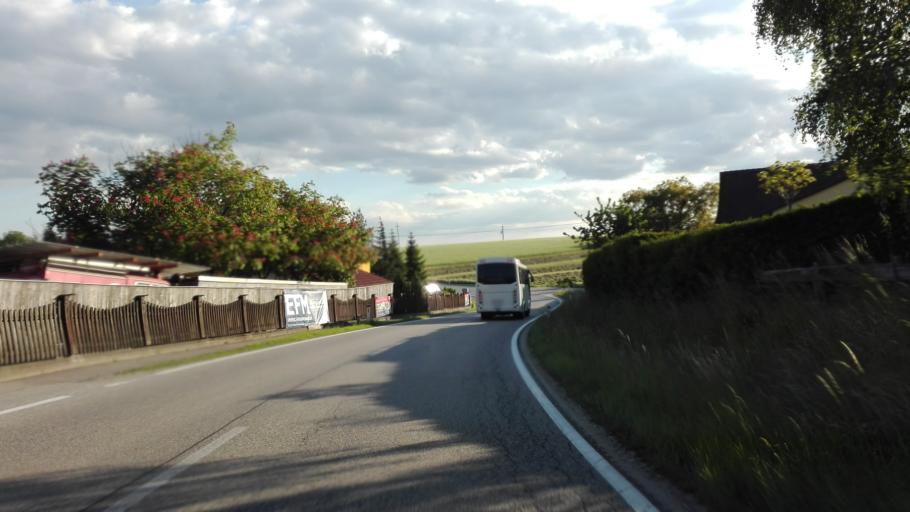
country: AT
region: Upper Austria
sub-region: Politischer Bezirk Urfahr-Umgebung
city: Engerwitzdorf
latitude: 48.3665
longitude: 14.5387
